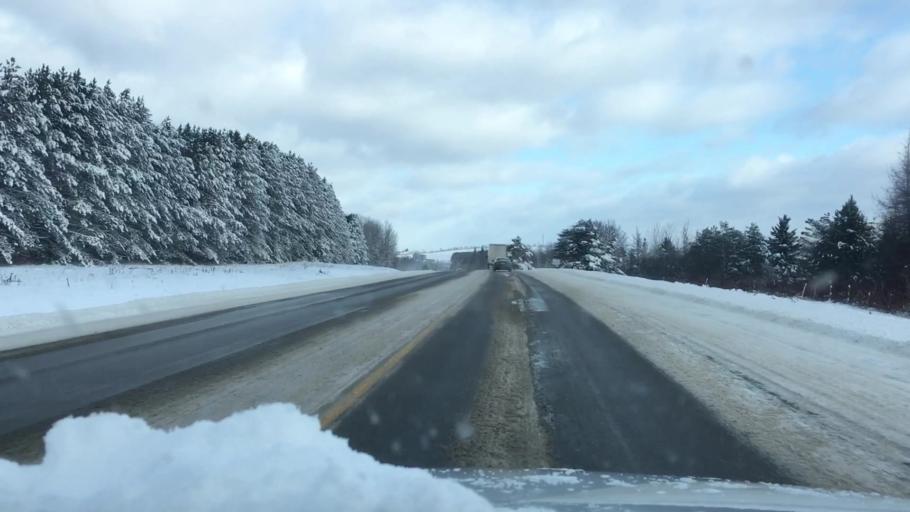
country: US
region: Maine
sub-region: Aroostook County
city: Caribou
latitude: 46.8202
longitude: -67.9939
